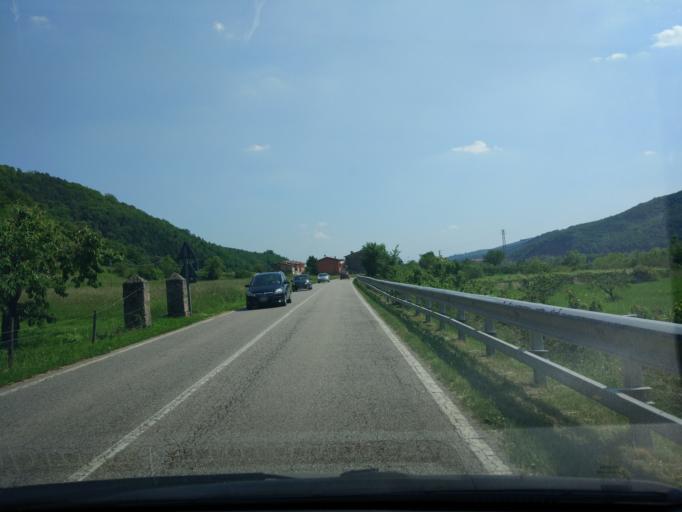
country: IT
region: Veneto
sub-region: Provincia di Verona
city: Badia Calavena
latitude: 45.5541
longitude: 11.1555
